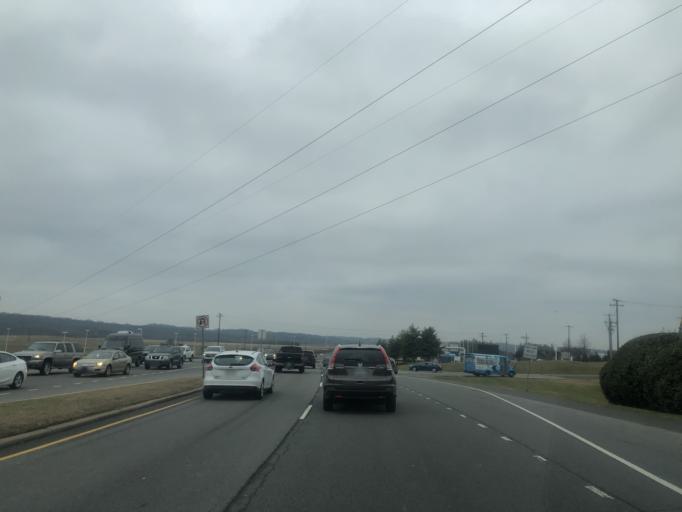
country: US
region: Tennessee
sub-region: Davidson County
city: Lakewood
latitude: 36.1394
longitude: -86.6662
